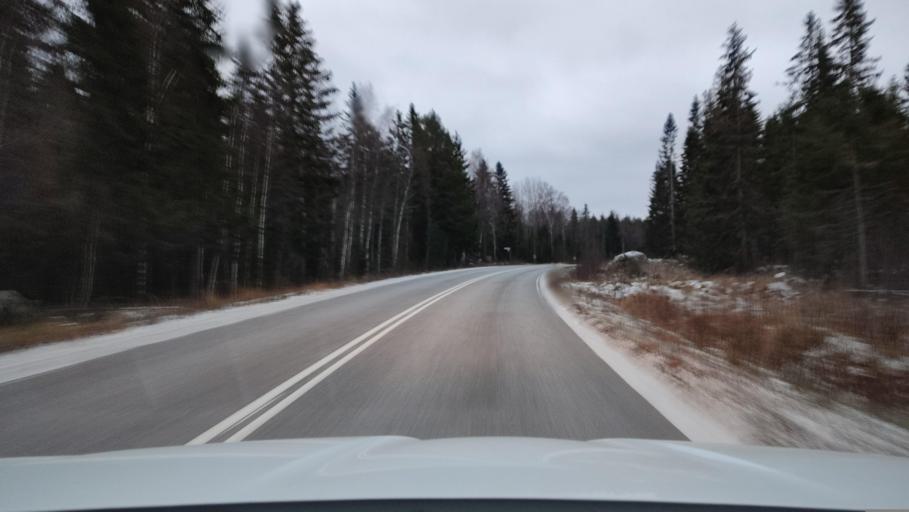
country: FI
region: Ostrobothnia
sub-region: Vaasa
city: Replot
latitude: 63.2654
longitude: 21.3555
